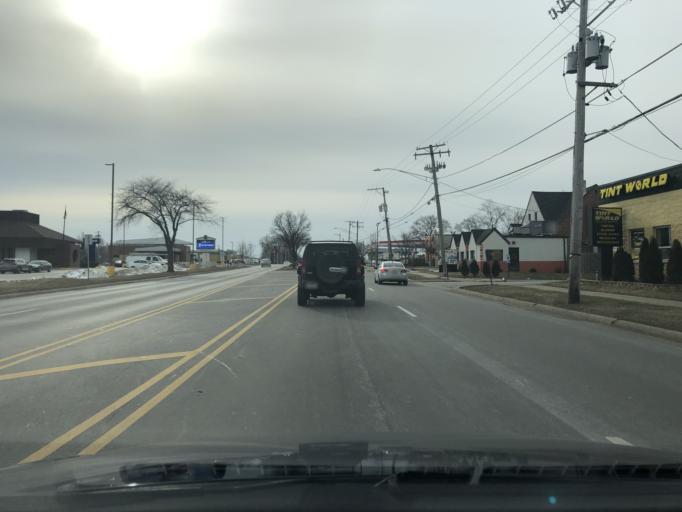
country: US
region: Illinois
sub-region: DuPage County
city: Bensenville
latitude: 41.9334
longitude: -87.9398
